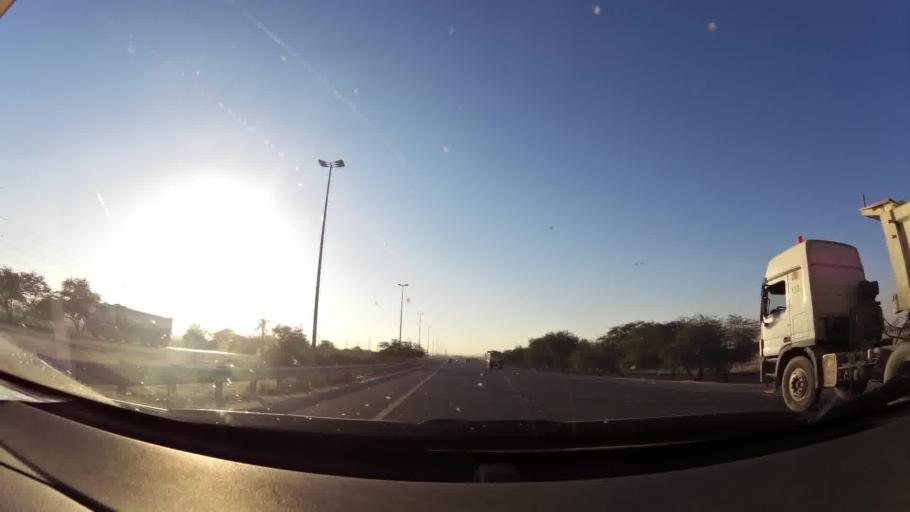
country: KW
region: Al Ahmadi
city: Al Fahahil
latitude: 28.8632
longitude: 48.2379
